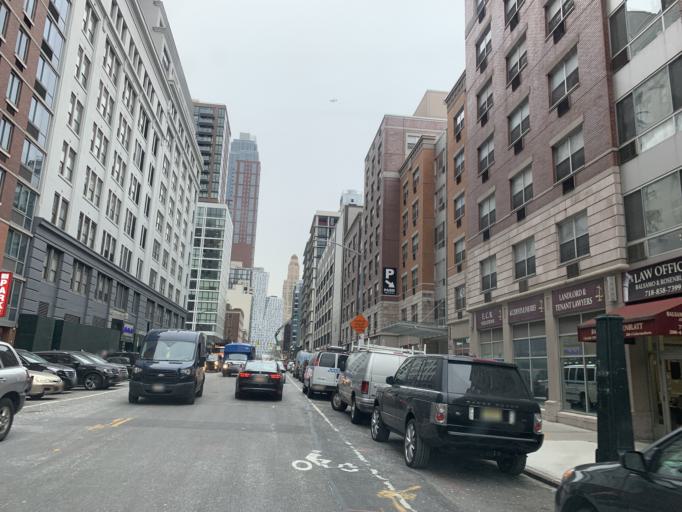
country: US
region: New York
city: New York City
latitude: 40.6886
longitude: -73.9855
